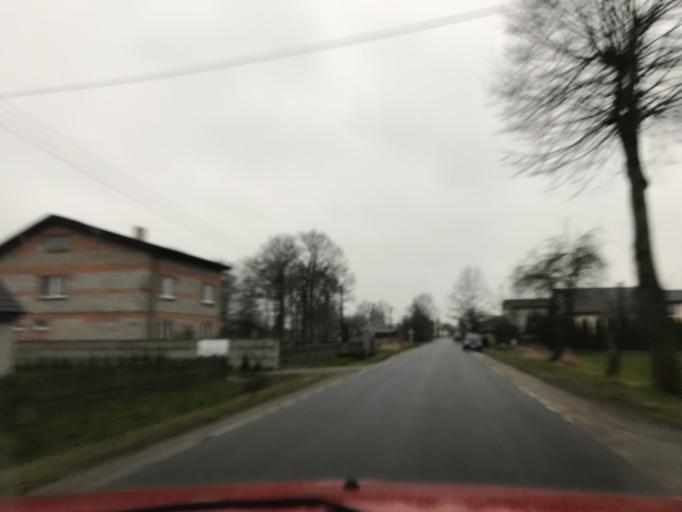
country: PL
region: Greater Poland Voivodeship
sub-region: Powiat ostrowski
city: Ostrow Wielkopolski
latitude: 51.7194
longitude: 17.7951
